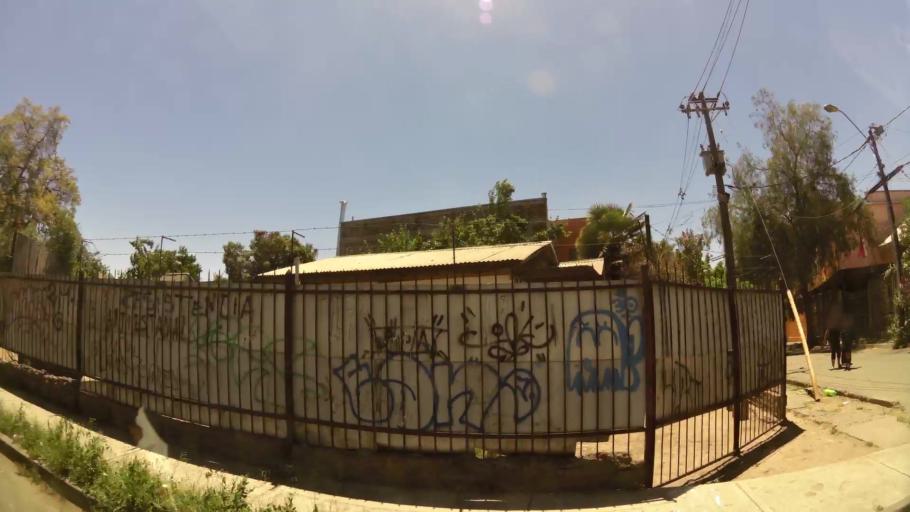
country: CL
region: Santiago Metropolitan
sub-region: Provincia de Maipo
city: San Bernardo
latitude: -33.5802
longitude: -70.6744
